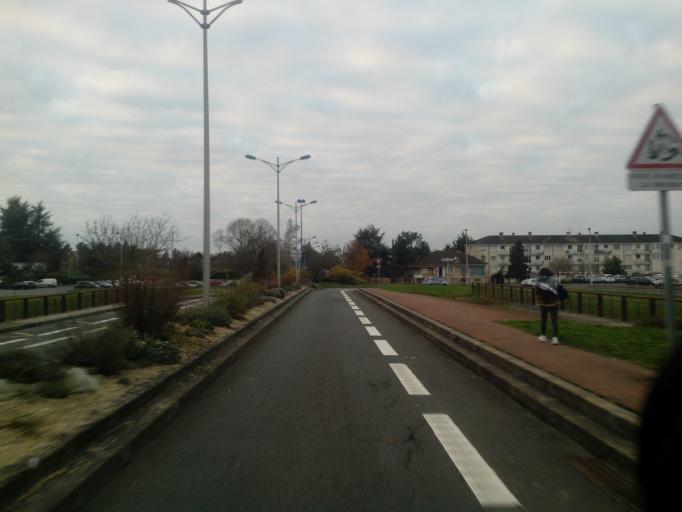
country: FR
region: Poitou-Charentes
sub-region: Departement de la Vienne
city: Saint-Benoit
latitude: 46.5701
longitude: 0.3790
